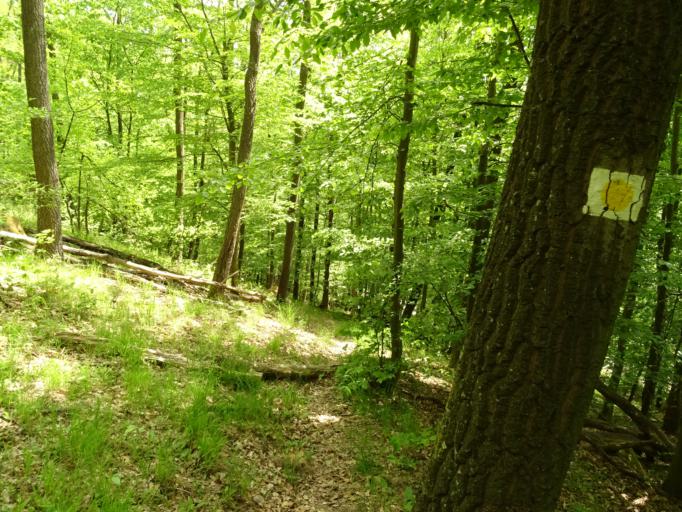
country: SK
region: Nitriansky
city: Sahy
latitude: 47.9936
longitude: 18.9532
